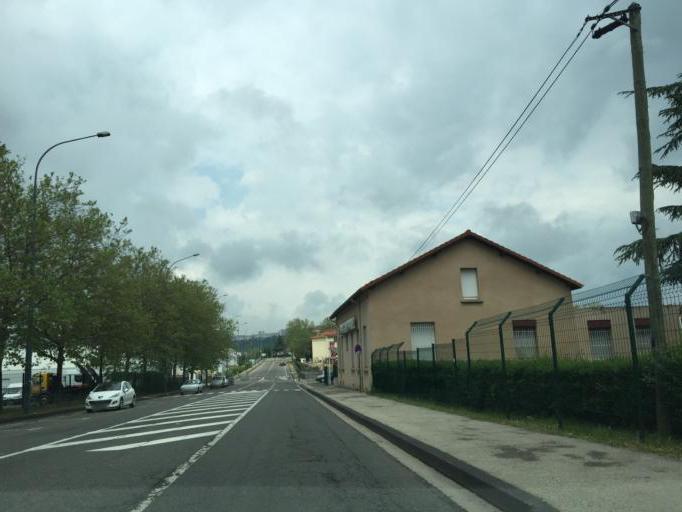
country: FR
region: Rhone-Alpes
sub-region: Departement de la Loire
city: Saint-Etienne
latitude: 45.4495
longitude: 4.3983
